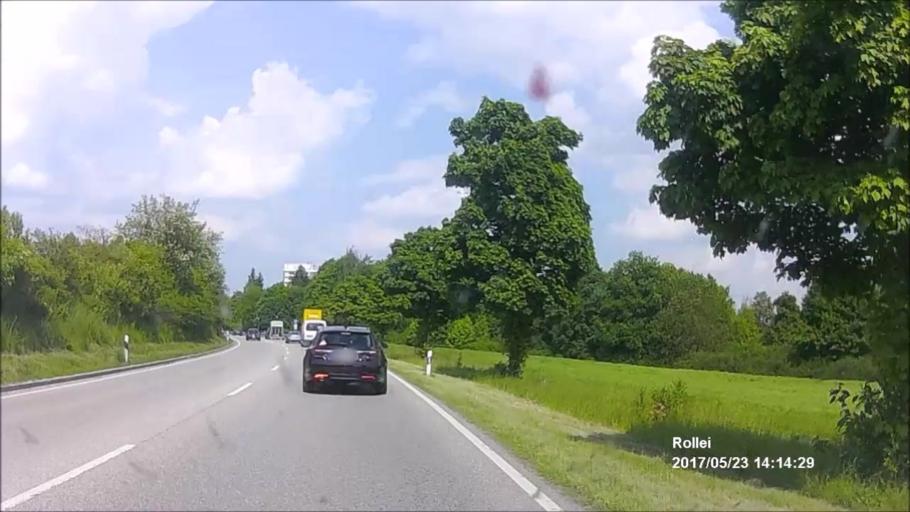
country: DE
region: Bavaria
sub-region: Upper Bavaria
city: Edling
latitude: 48.0589
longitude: 12.1943
